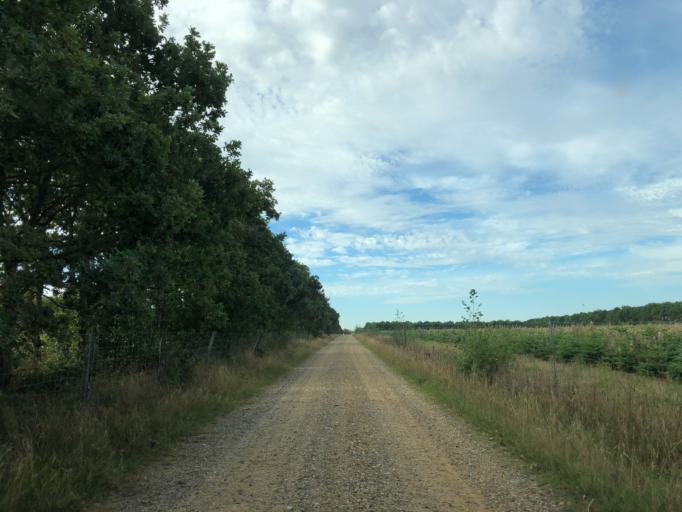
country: DK
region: Central Jutland
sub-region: Ringkobing-Skjern Kommune
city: Skjern
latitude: 56.0826
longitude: 8.4236
